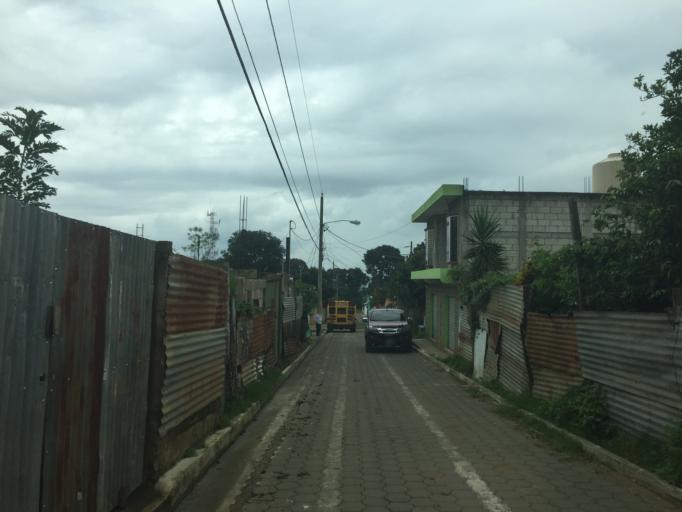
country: GT
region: Sacatepequez
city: Magdalena Milpas Altas
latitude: 14.5091
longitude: -90.6530
